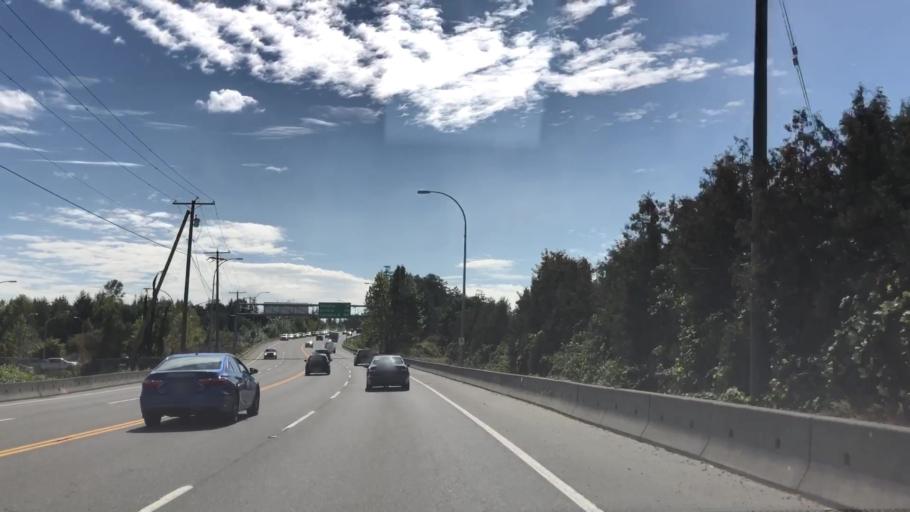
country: CA
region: British Columbia
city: Nanaimo
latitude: 49.1505
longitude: -123.8886
